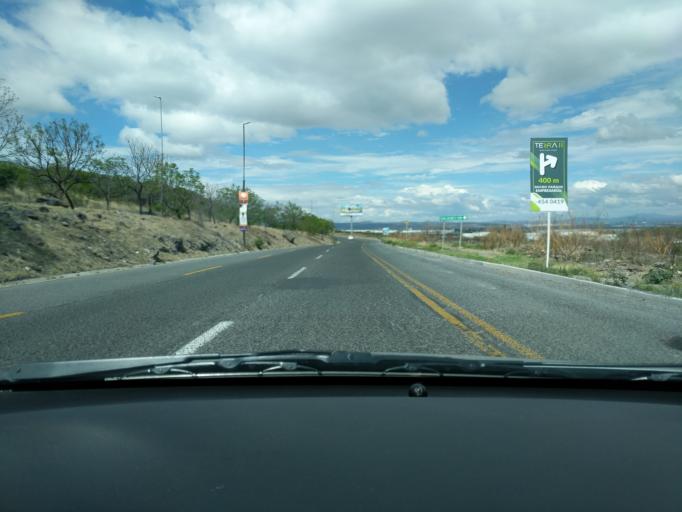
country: MX
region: Queretaro
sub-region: El Marques
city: La Pradera
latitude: 20.6624
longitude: -100.3343
